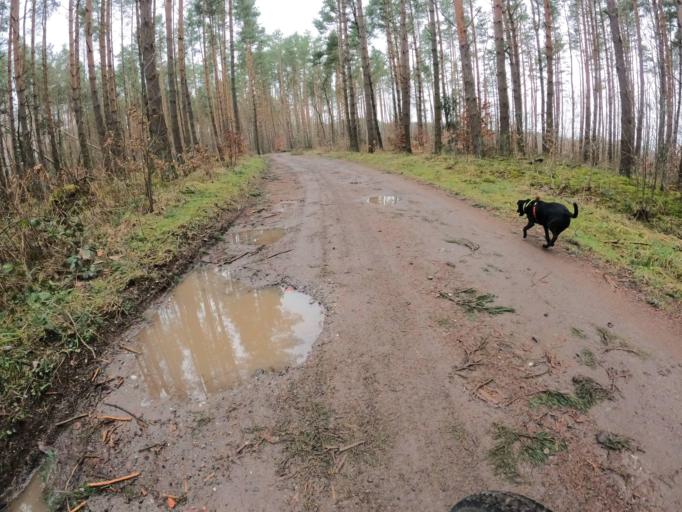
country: PL
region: West Pomeranian Voivodeship
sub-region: Powiat slawienski
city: Slawno
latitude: 54.2514
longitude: 16.6417
